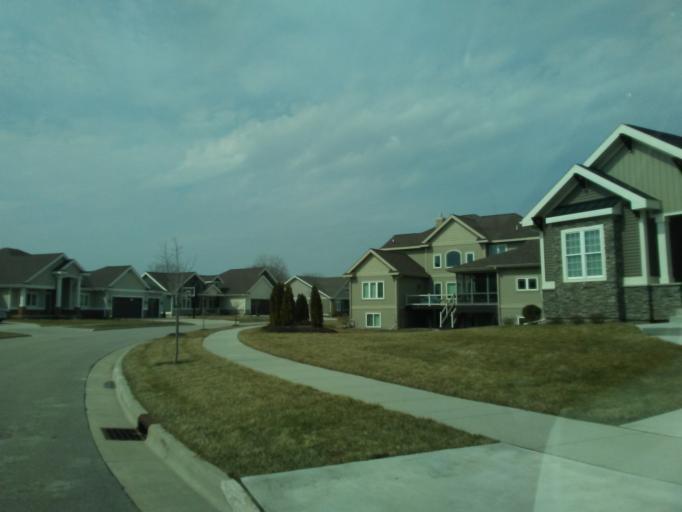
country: US
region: Wisconsin
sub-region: Dane County
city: Waunakee
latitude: 43.1687
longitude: -89.4523
